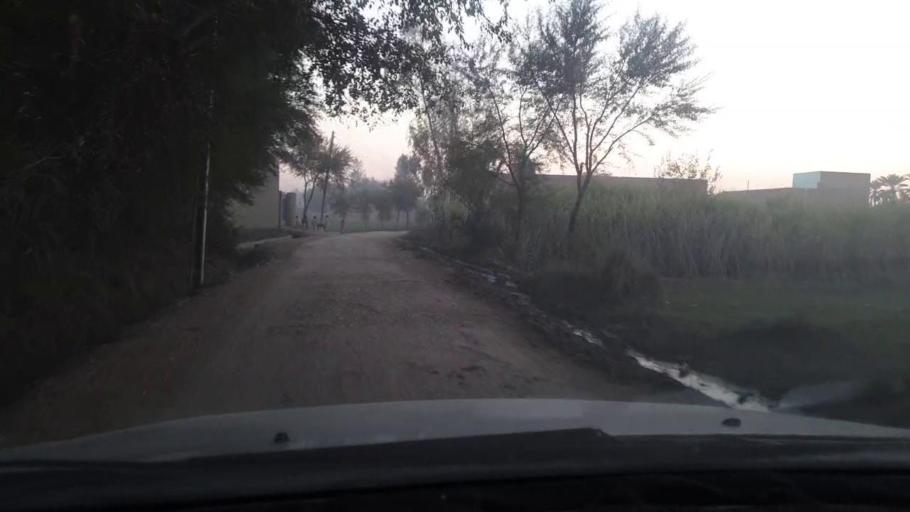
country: PK
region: Sindh
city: Ghotki
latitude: 28.0052
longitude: 69.3378
